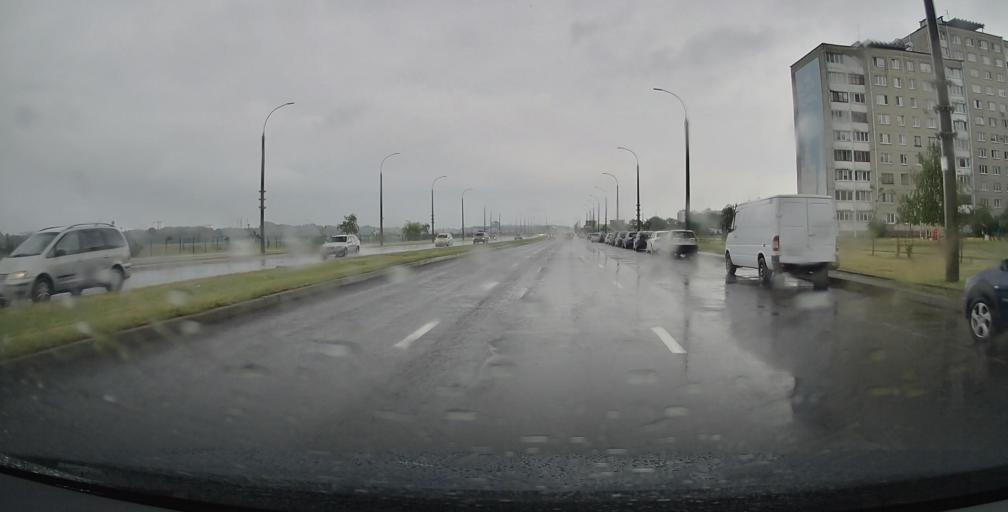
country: BY
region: Brest
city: Brest
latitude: 52.0816
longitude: 23.7490
